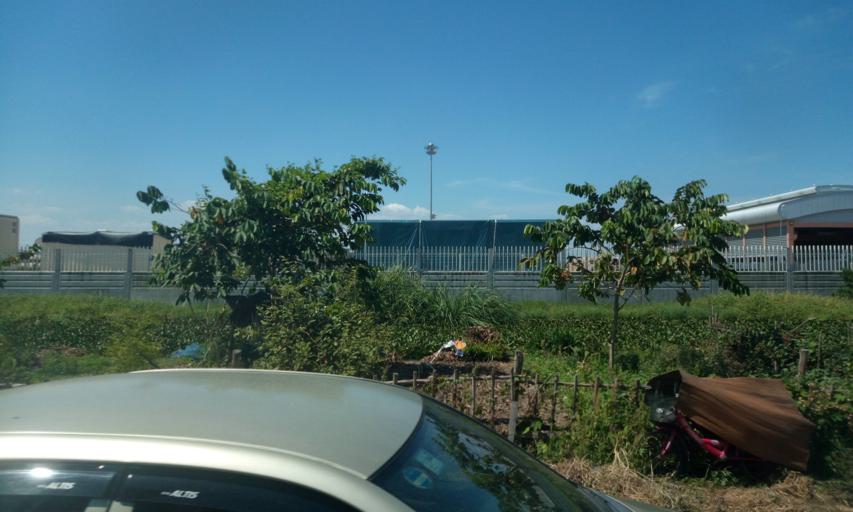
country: TH
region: Samut Prakan
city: Bang Bo District
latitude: 13.5563
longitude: 100.7697
